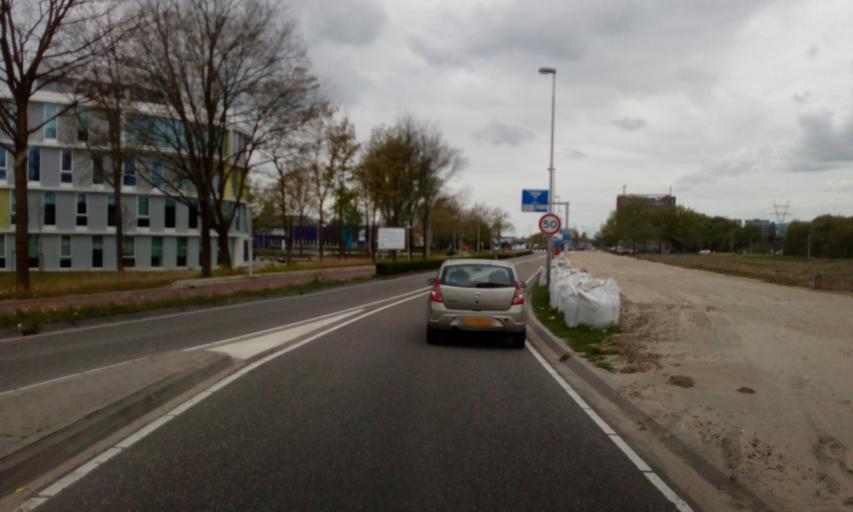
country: NL
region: South Holland
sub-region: Gemeente Barendrecht
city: Barendrecht
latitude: 51.8627
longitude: 4.5403
